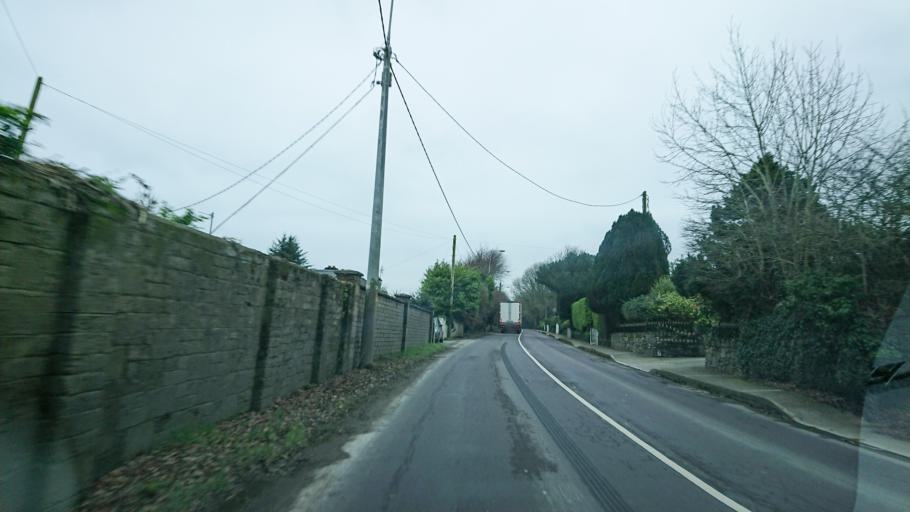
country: IE
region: Munster
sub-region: County Cork
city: Bandon
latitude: 51.7470
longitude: -8.7519
